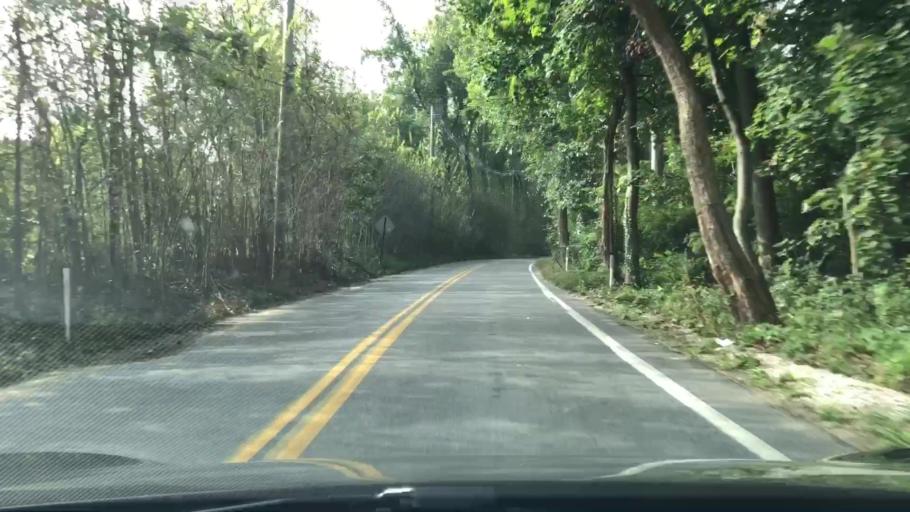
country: US
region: Pennsylvania
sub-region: Delaware County
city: Wayne
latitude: 40.0139
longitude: -75.3739
